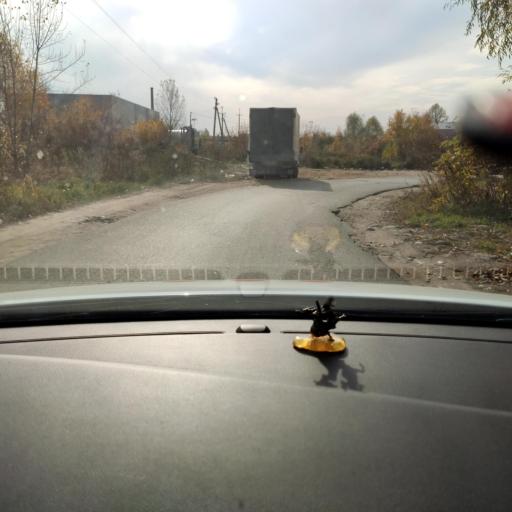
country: RU
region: Tatarstan
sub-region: Gorod Kazan'
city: Kazan
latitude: 55.7524
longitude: 49.1156
